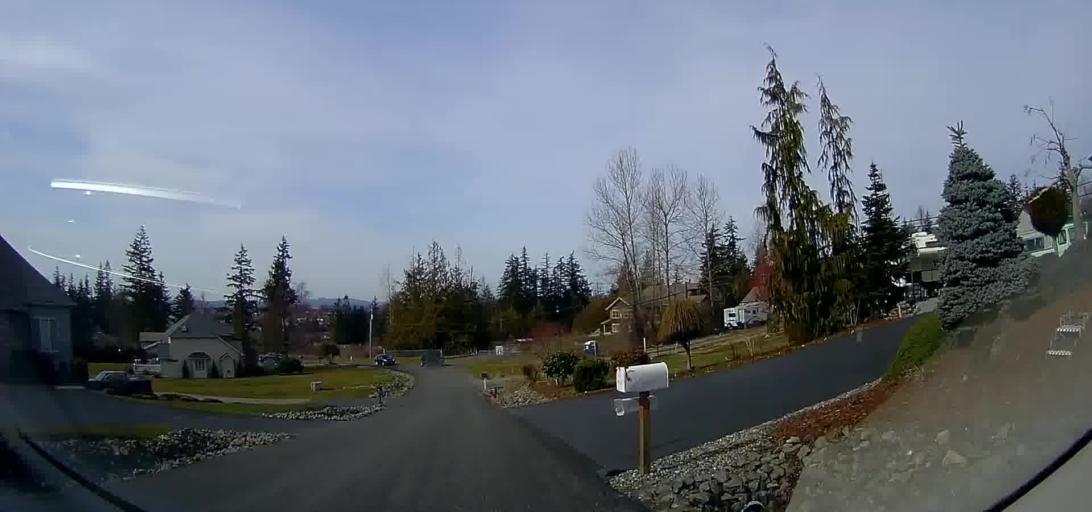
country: US
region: Washington
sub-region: Skagit County
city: Mount Vernon
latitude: 48.3952
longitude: -122.3185
